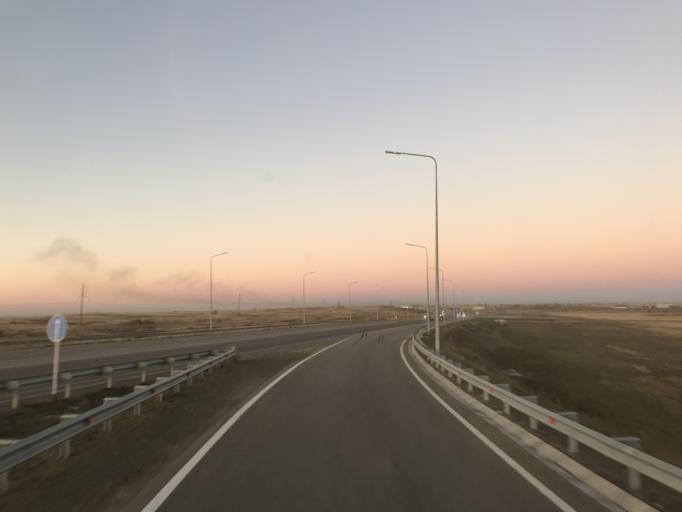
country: KZ
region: Astana Qalasy
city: Astana
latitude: 51.2349
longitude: 71.5577
